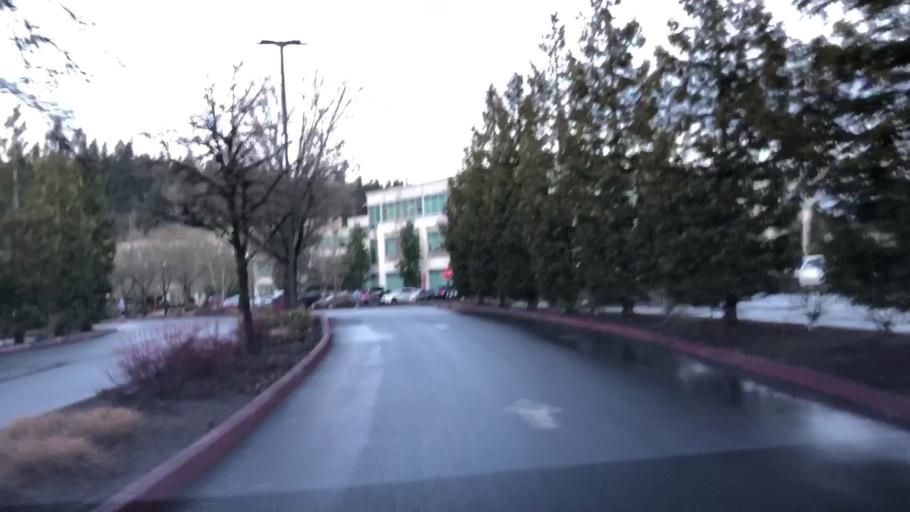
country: US
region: Washington
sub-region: King County
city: Bothell
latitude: 47.7748
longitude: -122.1869
